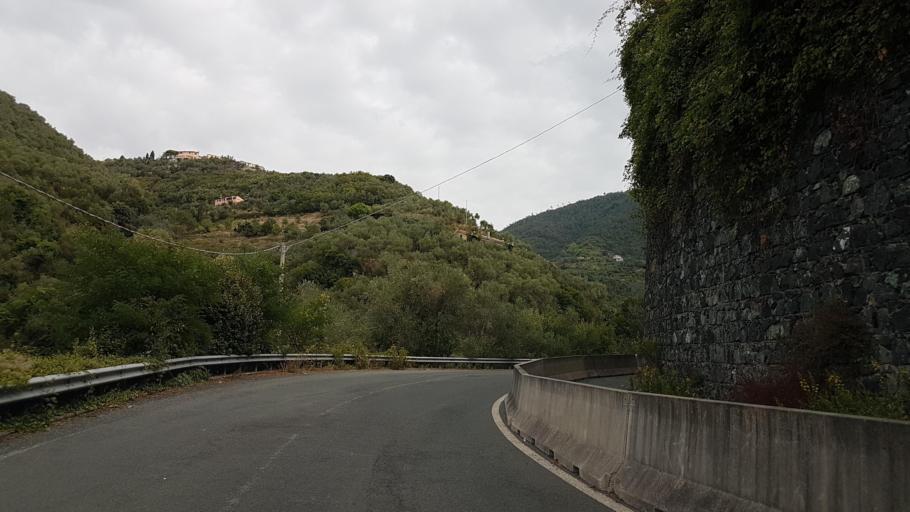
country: IT
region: Liguria
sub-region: Provincia di La Spezia
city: Levanto
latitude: 44.1875
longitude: 9.6218
